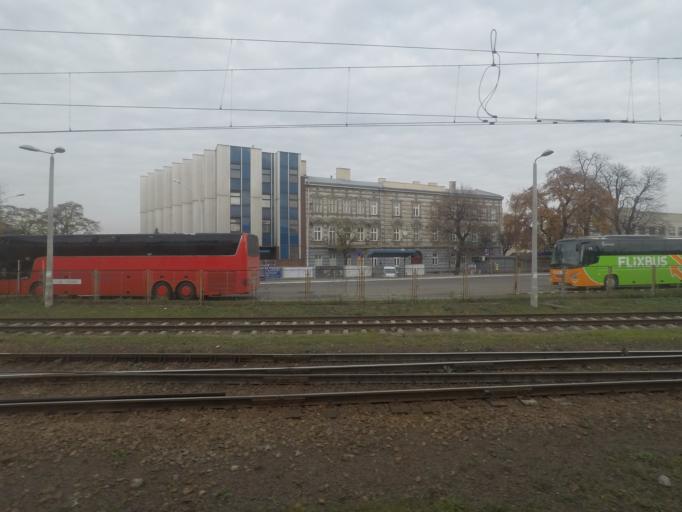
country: PL
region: Subcarpathian Voivodeship
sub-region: Przemysl
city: Przemysl
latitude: 49.7844
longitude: 22.7737
